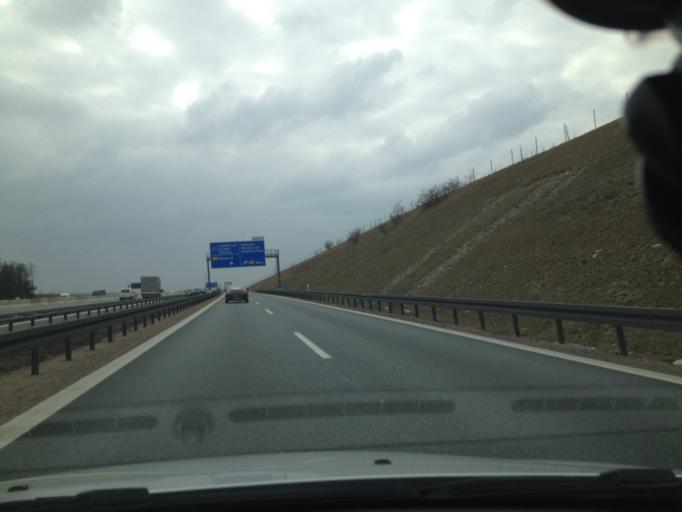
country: DE
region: Bavaria
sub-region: Regierungsbezirk Unterfranken
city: Biebelried
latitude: 49.7745
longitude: 10.0791
